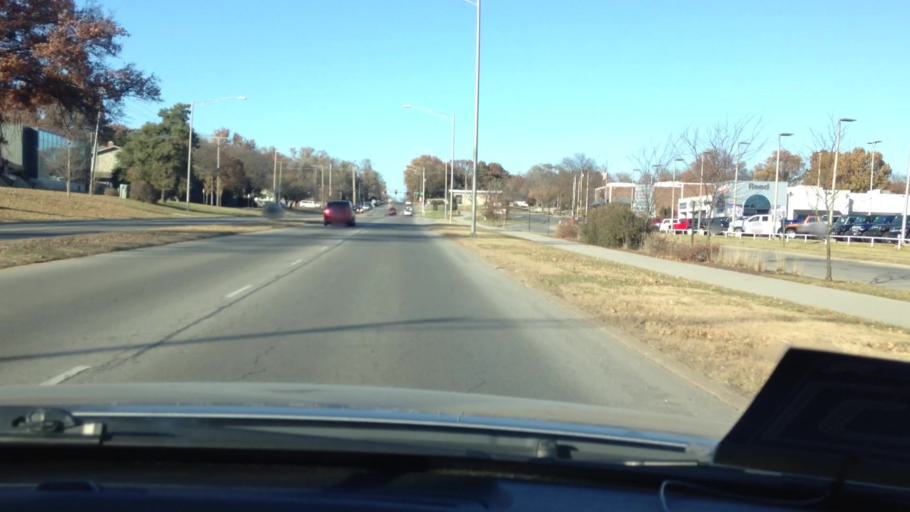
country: US
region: Kansas
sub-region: Johnson County
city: Overland Park
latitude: 38.9641
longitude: -94.6668
